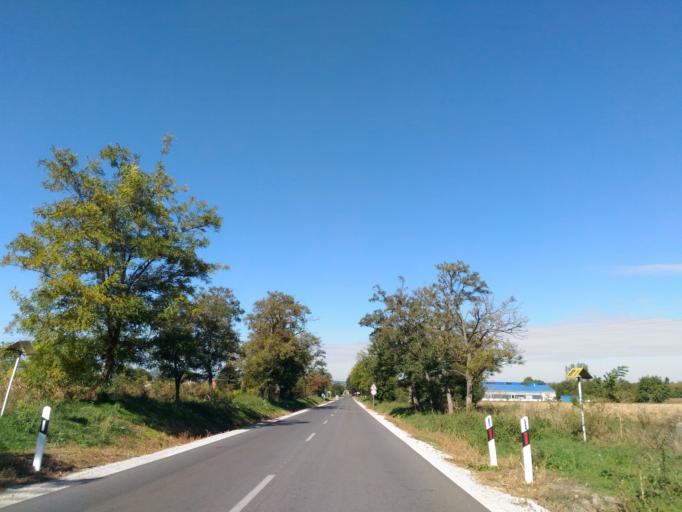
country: HU
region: Fejer
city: Kapolnasnyek
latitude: 47.2179
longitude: 18.6776
